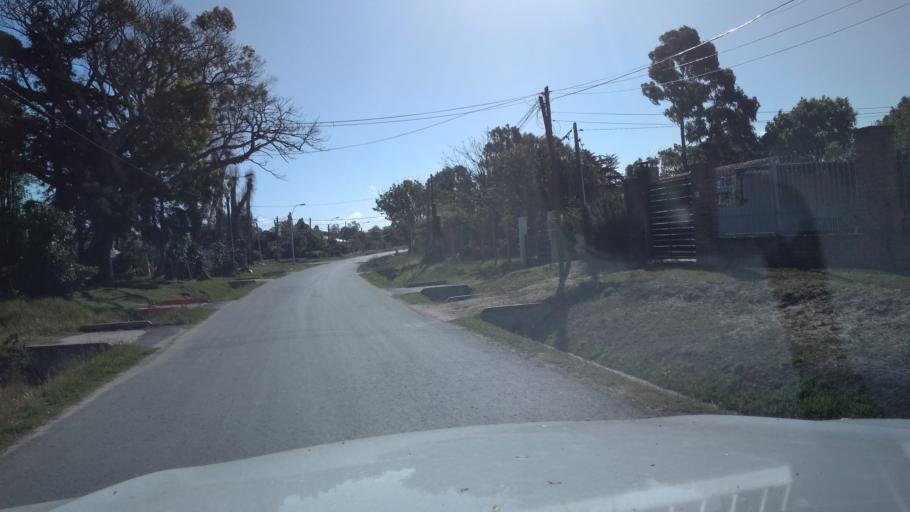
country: UY
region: Canelones
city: Colonia Nicolich
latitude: -34.8301
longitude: -55.9790
